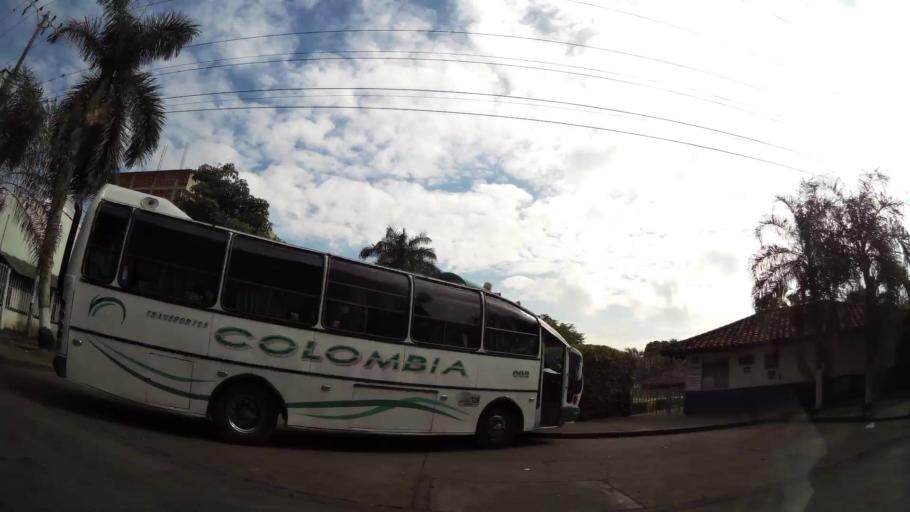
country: CO
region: Valle del Cauca
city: Cali
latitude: 3.4793
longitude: -76.4911
